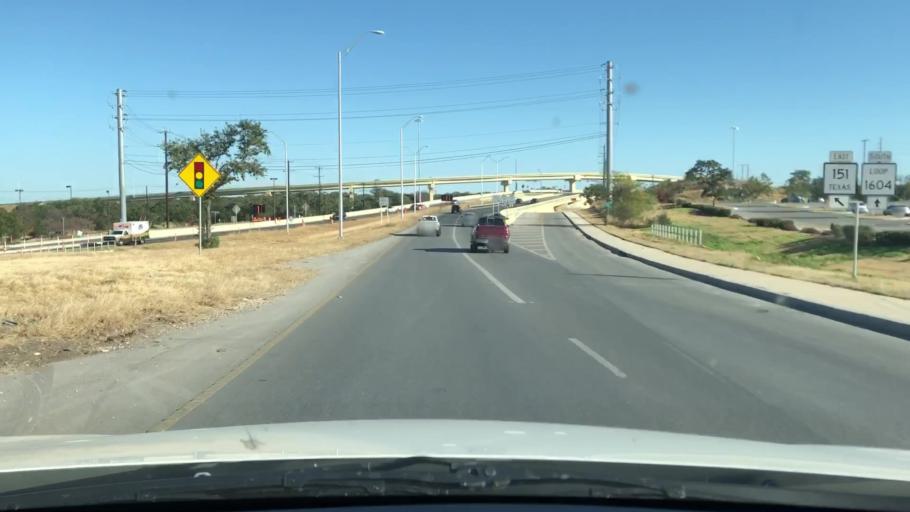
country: US
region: Texas
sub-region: Bexar County
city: Helotes
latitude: 29.4858
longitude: -98.7144
